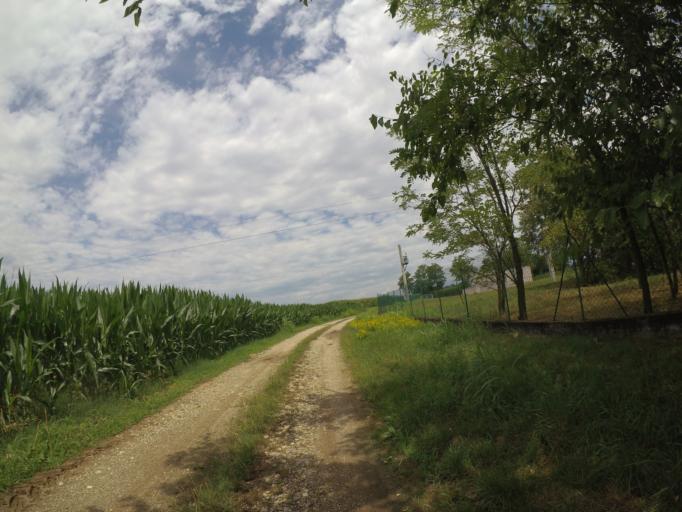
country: IT
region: Friuli Venezia Giulia
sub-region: Provincia di Udine
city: Bertiolo
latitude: 45.9648
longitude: 13.0642
